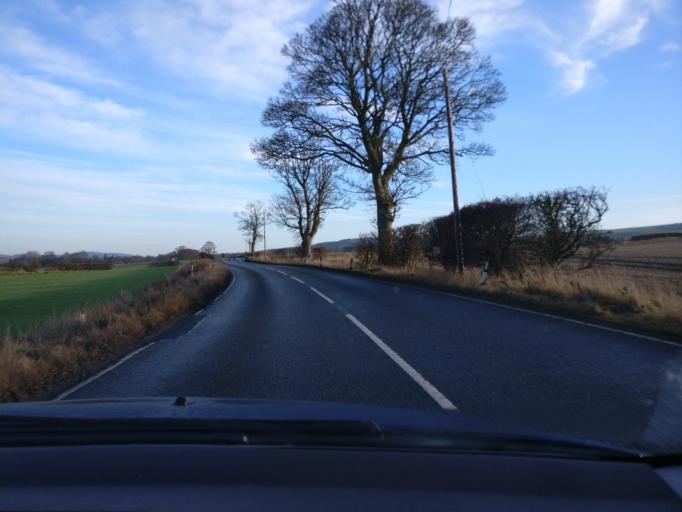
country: GB
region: Scotland
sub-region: The Scottish Borders
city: Saint Boswells
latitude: 55.4662
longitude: -2.6628
